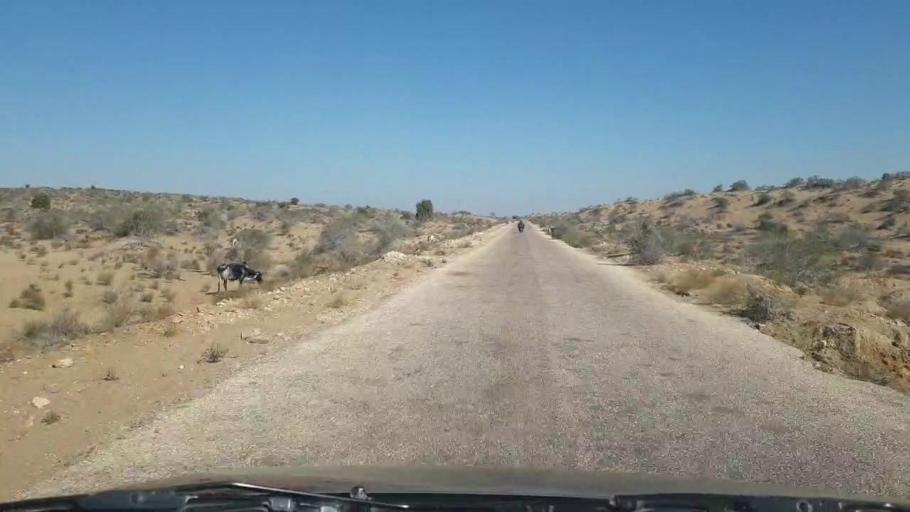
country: PK
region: Sindh
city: Bozdar
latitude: 27.0033
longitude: 68.8671
